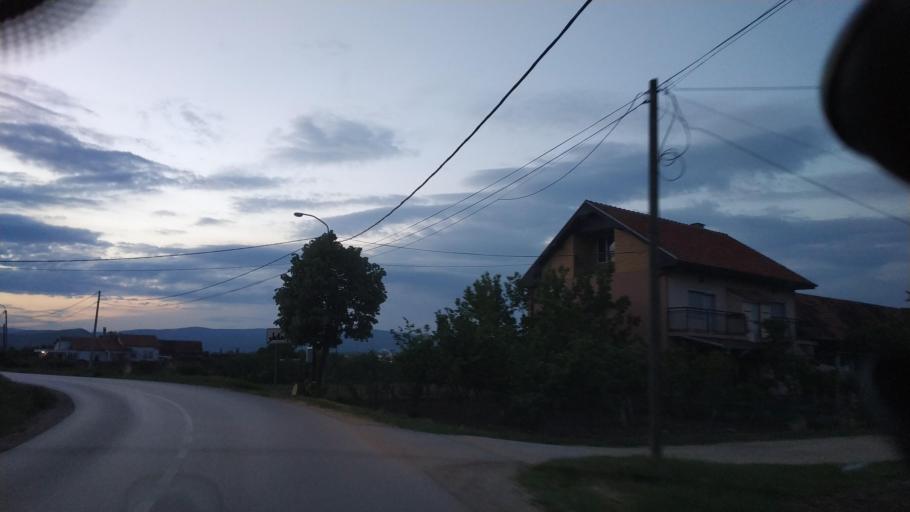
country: RS
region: Central Serbia
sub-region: Nisavski Okrug
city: Merosina
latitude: 43.2878
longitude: 21.7176
